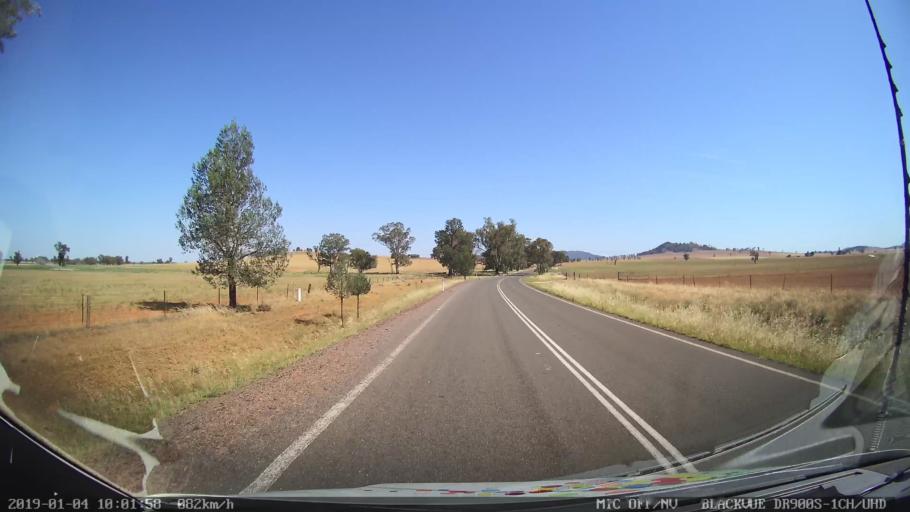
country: AU
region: New South Wales
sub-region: Cabonne
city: Canowindra
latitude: -33.4821
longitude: 148.3666
